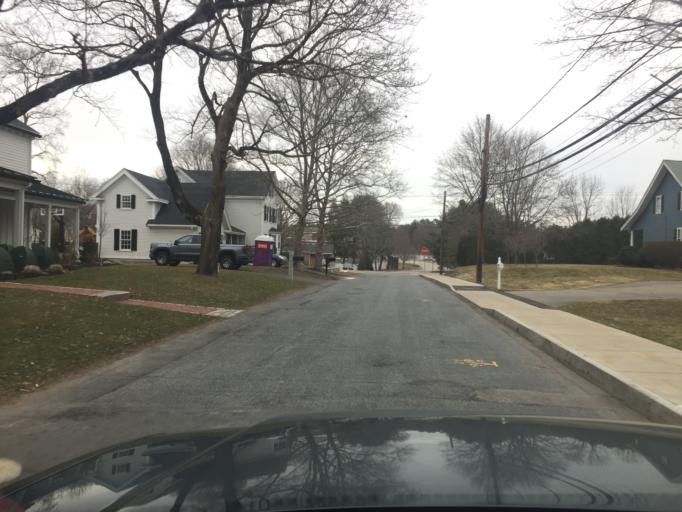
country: US
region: Massachusetts
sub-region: Norfolk County
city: Medfield
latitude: 42.1829
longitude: -71.2994
